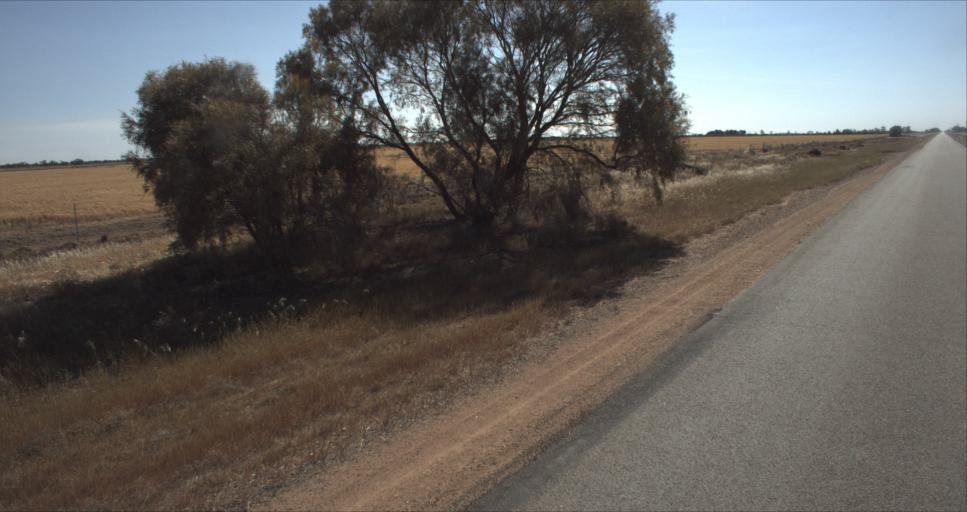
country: AU
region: New South Wales
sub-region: Leeton
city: Leeton
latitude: -34.4969
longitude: 146.3904
